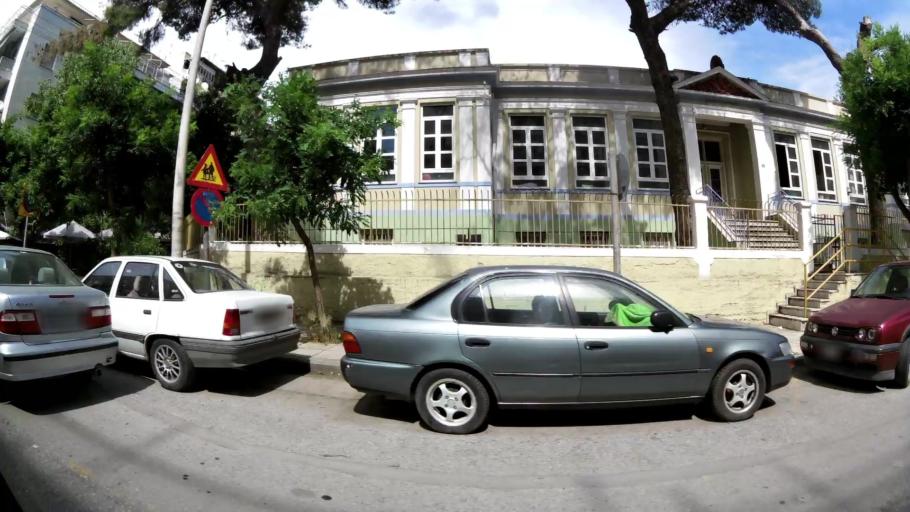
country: GR
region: Central Macedonia
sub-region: Nomos Thessalonikis
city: Triandria
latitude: 40.6039
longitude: 22.9586
